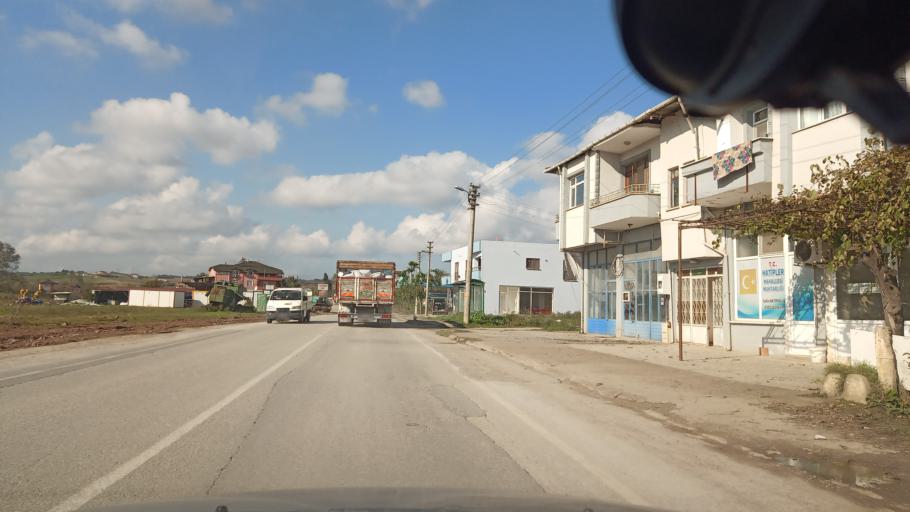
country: TR
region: Sakarya
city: Kaynarca
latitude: 41.0388
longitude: 30.2951
